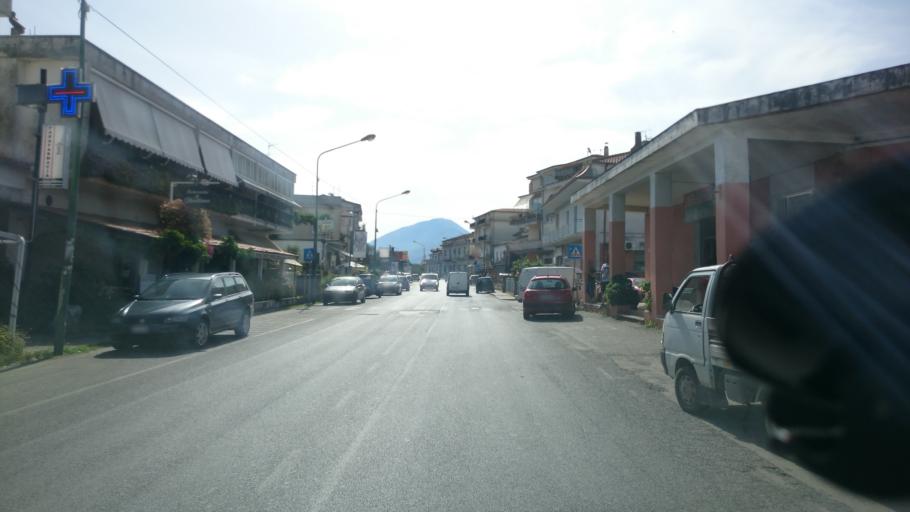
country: IT
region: Campania
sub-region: Provincia di Salerno
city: Policastro Bussentino
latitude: 40.0740
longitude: 15.5210
